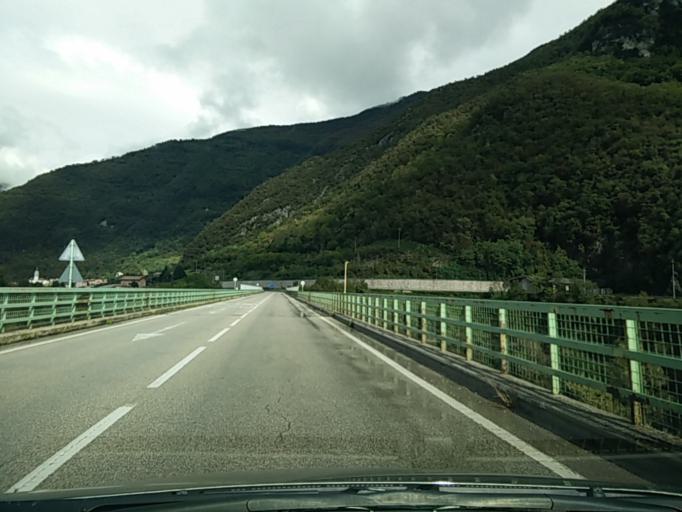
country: IT
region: Veneto
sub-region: Provincia di Belluno
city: Vas
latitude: 45.9284
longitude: 11.9408
